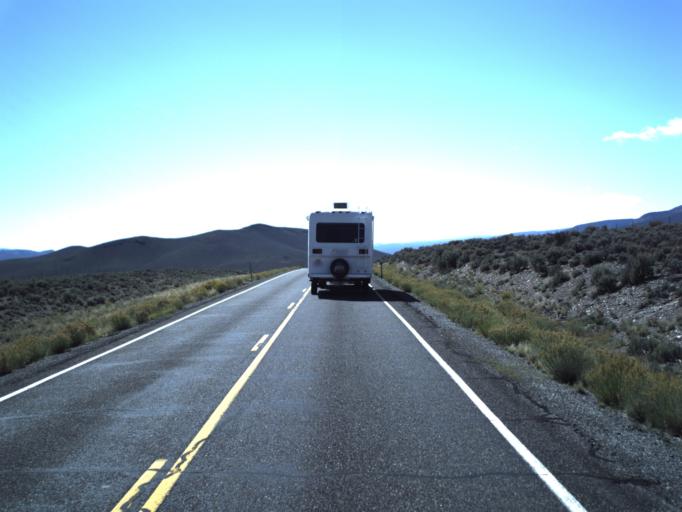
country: US
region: Utah
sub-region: Piute County
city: Junction
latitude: 38.3093
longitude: -111.9684
